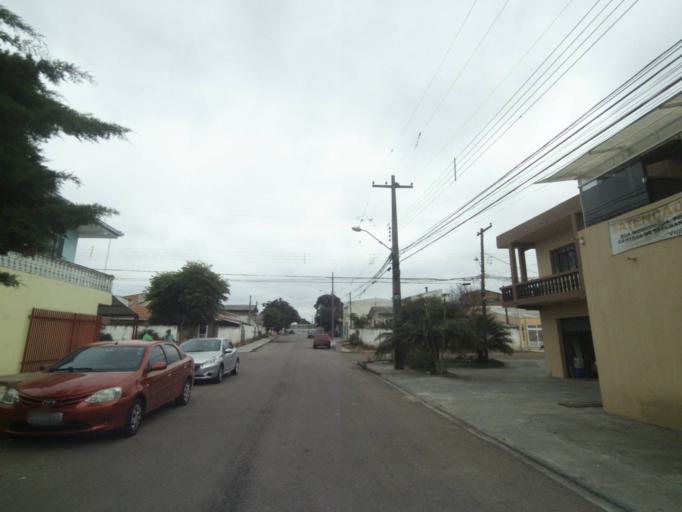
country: BR
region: Parana
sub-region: Sao Jose Dos Pinhais
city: Sao Jose dos Pinhais
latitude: -25.5437
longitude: -49.2591
